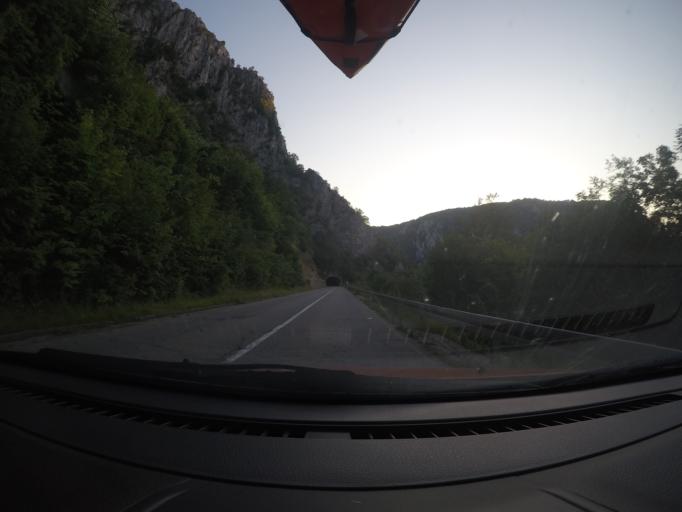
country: RO
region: Mehedinti
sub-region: Comuna Dubova
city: Dubova
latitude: 44.6340
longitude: 22.2966
